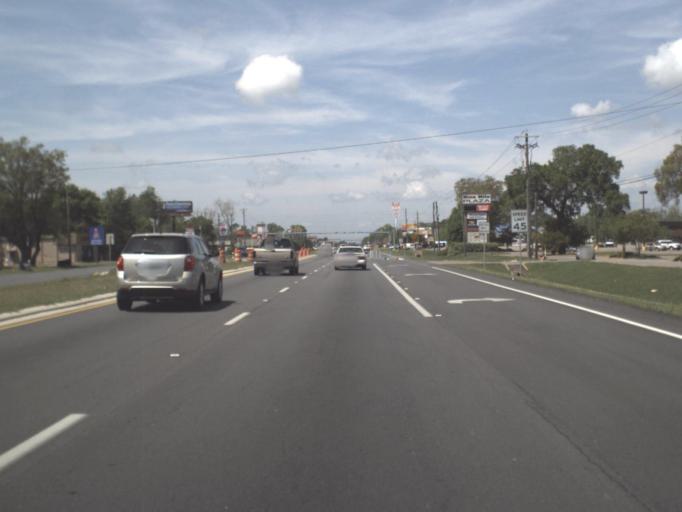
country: US
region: Florida
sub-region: Escambia County
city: Ensley
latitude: 30.5329
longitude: -87.2587
